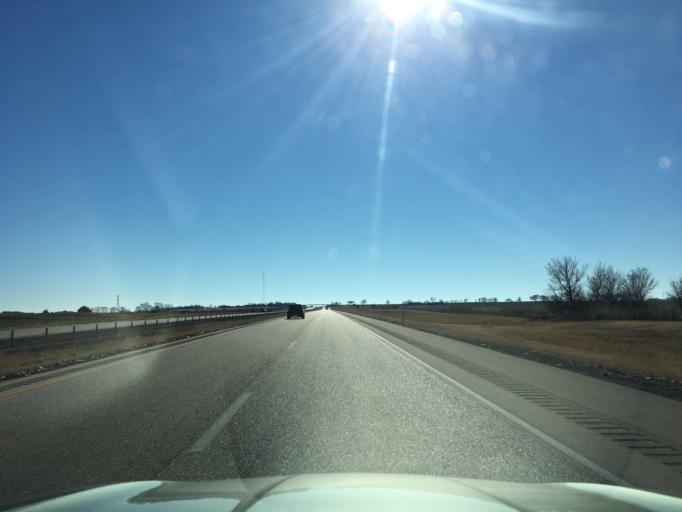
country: US
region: Oklahoma
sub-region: Kay County
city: Blackwell
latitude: 36.8819
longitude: -97.3516
